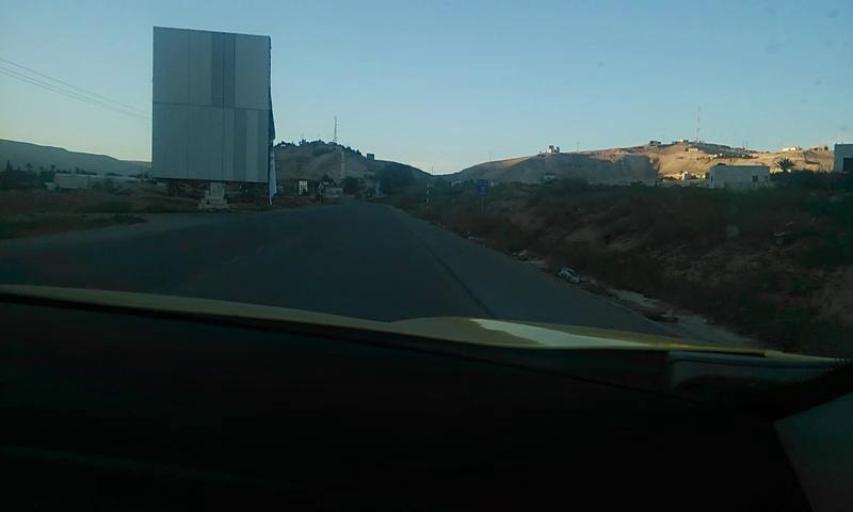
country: PS
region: West Bank
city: An Nuway`imah
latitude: 31.8916
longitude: 35.4308
